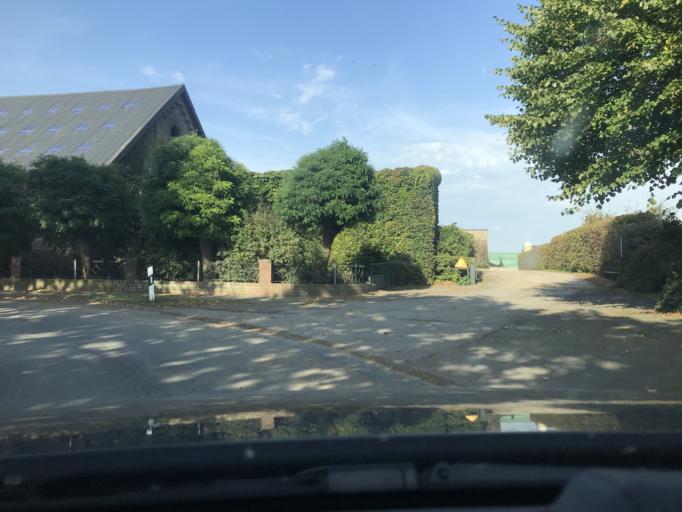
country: DE
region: North Rhine-Westphalia
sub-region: Regierungsbezirk Dusseldorf
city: Emmerich
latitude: 51.7895
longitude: 6.2331
